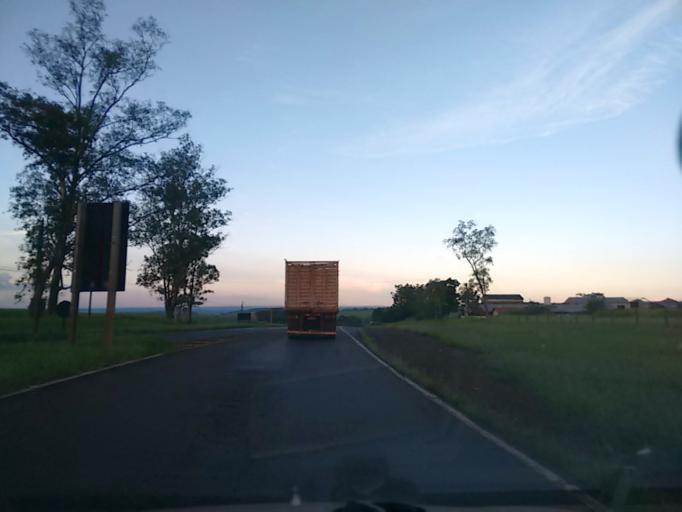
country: BR
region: Sao Paulo
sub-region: Jau
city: Jau
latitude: -22.1533
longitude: -48.4716
